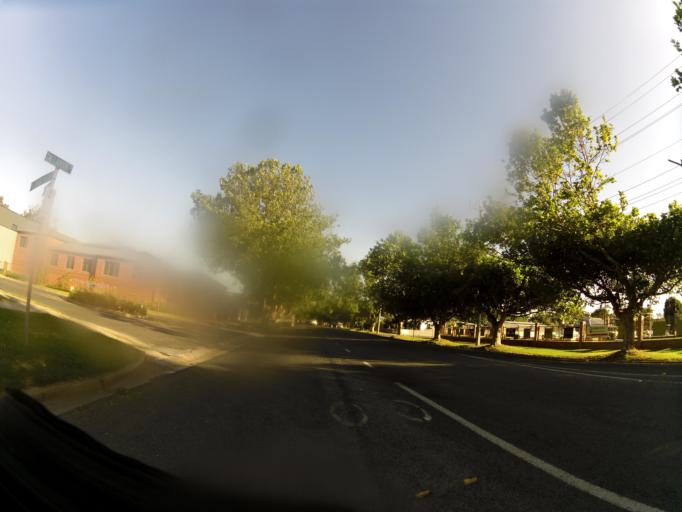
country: AU
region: Victoria
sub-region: Murrindindi
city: Kinglake West
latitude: -37.0222
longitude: 145.1316
